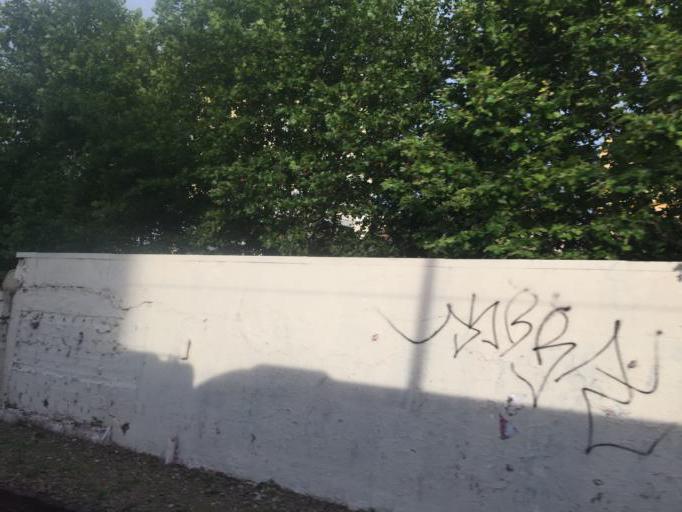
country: AR
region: Buenos Aires
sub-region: Partido de Lanus
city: Lanus
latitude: -34.7061
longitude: -58.3900
